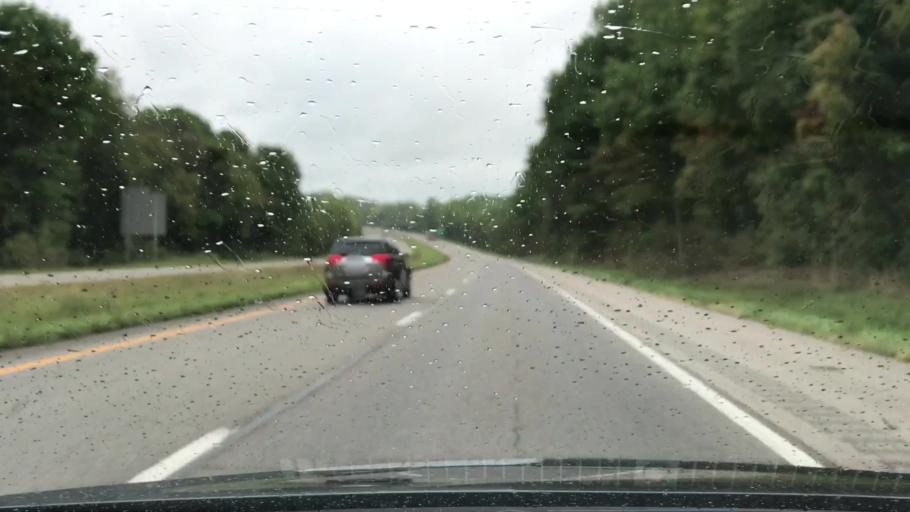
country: US
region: Kentucky
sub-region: Barren County
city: Glasgow
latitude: 36.9728
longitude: -85.9171
